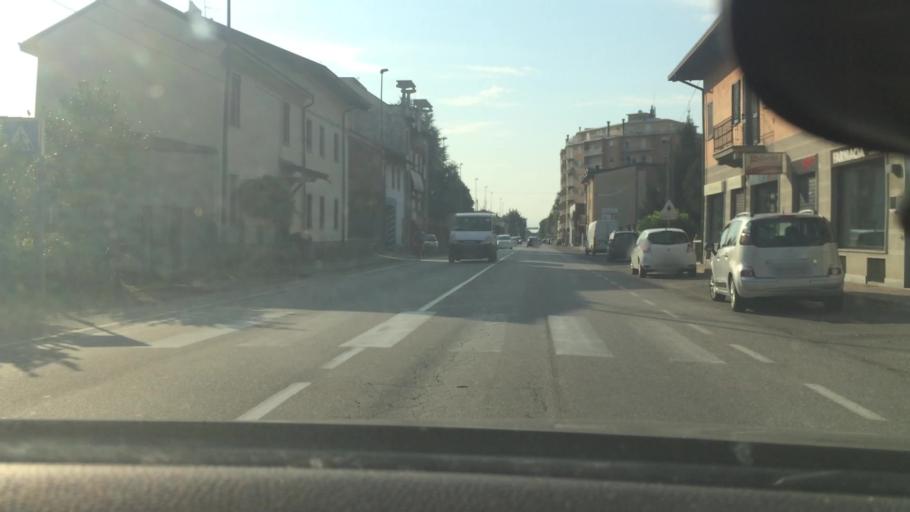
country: IT
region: Lombardy
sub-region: Provincia di Varese
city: Gerenzano
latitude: 45.6413
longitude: 9.0032
